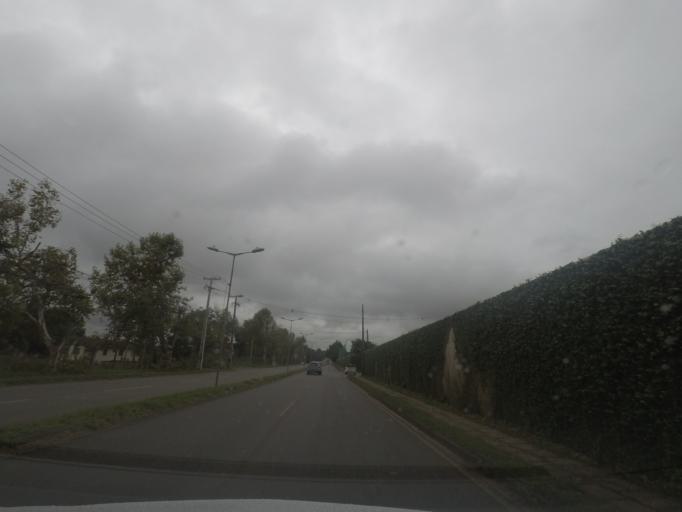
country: BR
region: Parana
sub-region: Pinhais
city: Pinhais
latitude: -25.3927
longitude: -49.1676
